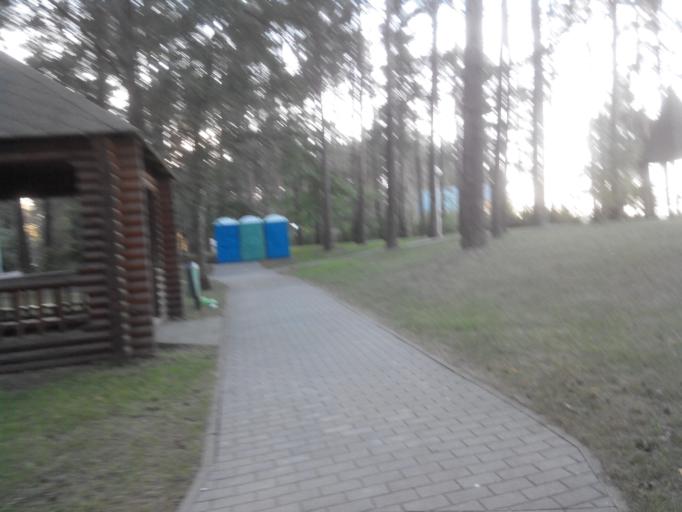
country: BY
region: Minsk
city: Narach
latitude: 54.8380
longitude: 26.7150
